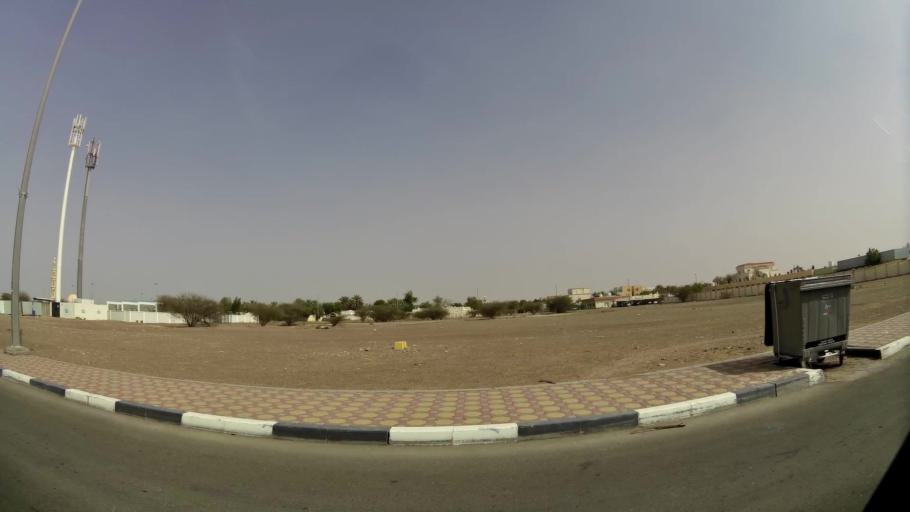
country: AE
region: Abu Dhabi
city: Al Ain
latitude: 24.1855
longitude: 55.6176
